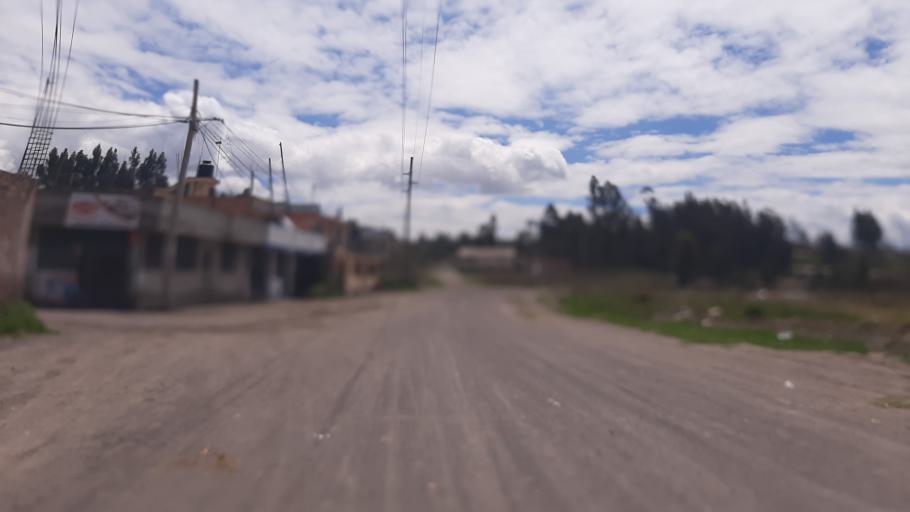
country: EC
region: Chimborazo
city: Riobamba
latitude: -1.6508
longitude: -78.6405
